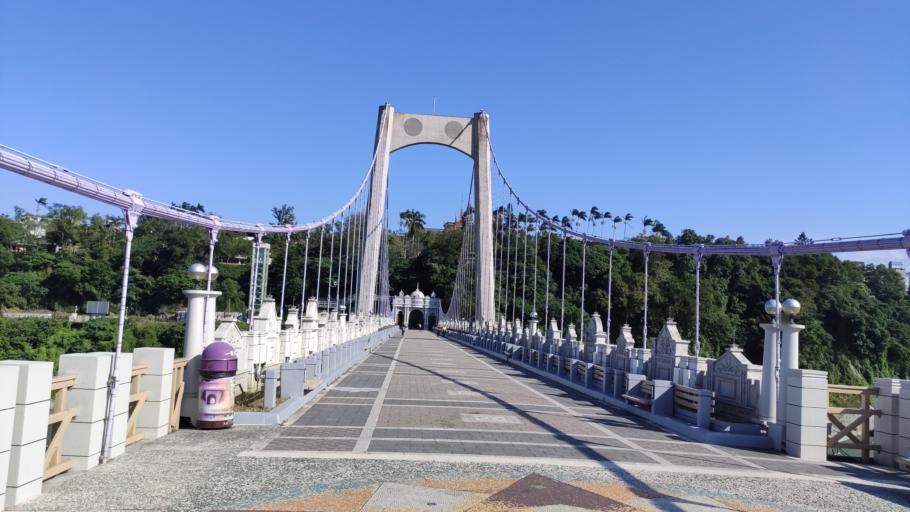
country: TW
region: Taiwan
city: Daxi
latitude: 24.8851
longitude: 121.2827
